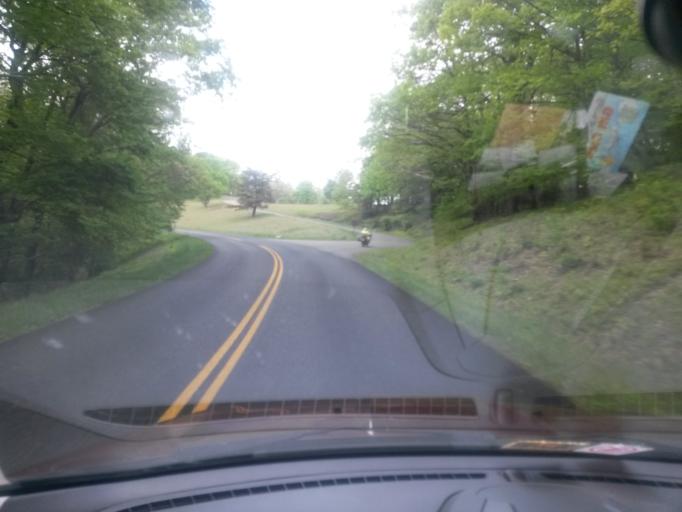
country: US
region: Virginia
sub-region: Floyd County
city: Floyd
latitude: 36.8218
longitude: -80.3427
